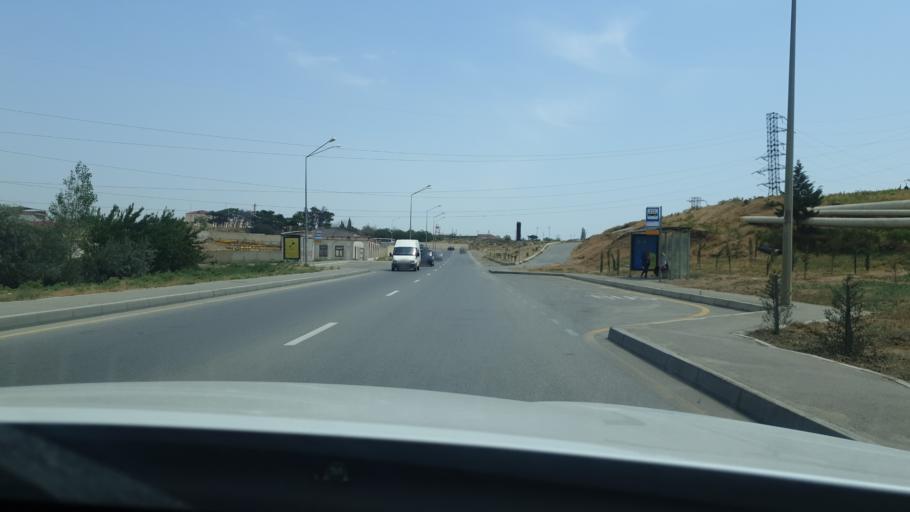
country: AZ
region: Baki
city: Qaracuxur
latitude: 40.3925
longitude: 49.9855
